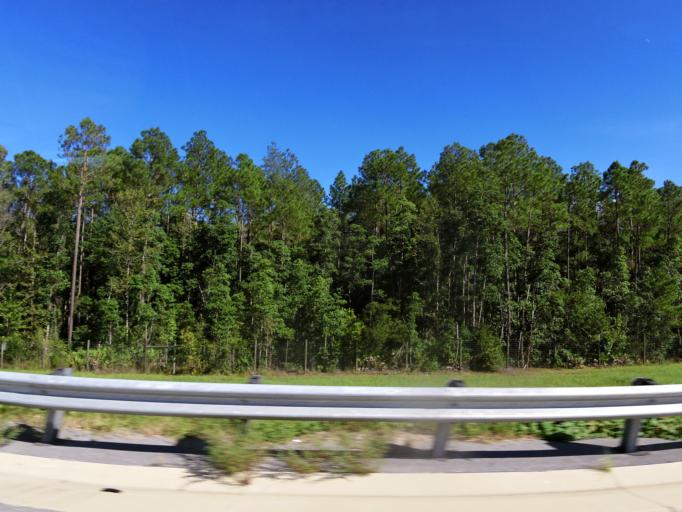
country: US
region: Florida
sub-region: Saint Johns County
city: Palm Valley
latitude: 30.1306
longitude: -81.5101
